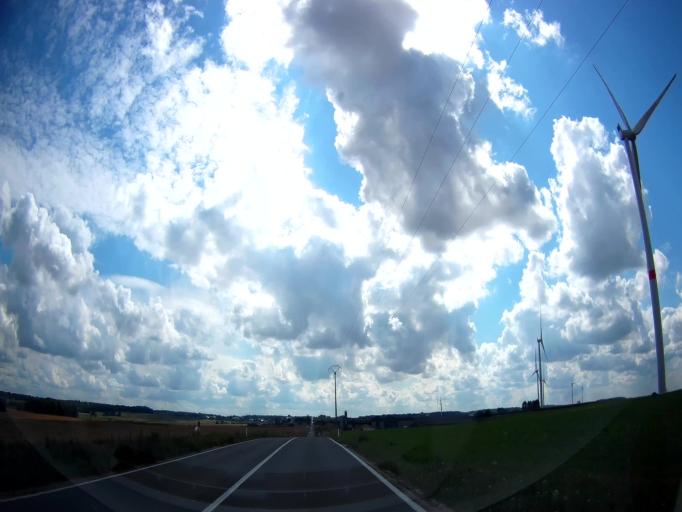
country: BE
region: Wallonia
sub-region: Province de Namur
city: Ohey
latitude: 50.4218
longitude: 5.1242
